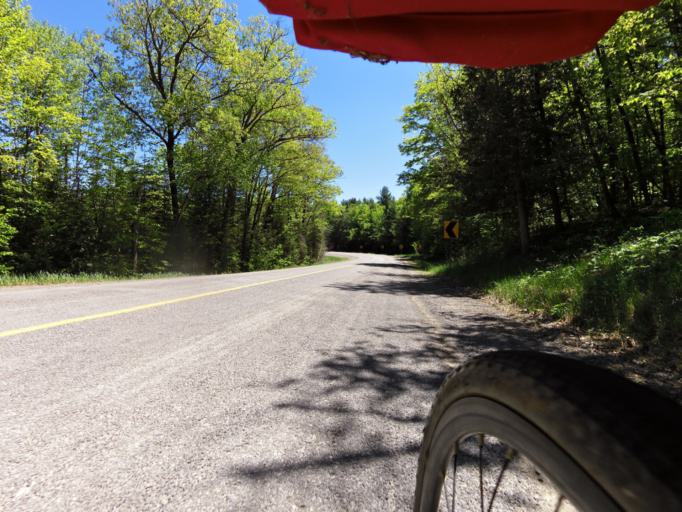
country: CA
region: Ontario
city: Arnprior
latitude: 45.1610
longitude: -76.4398
